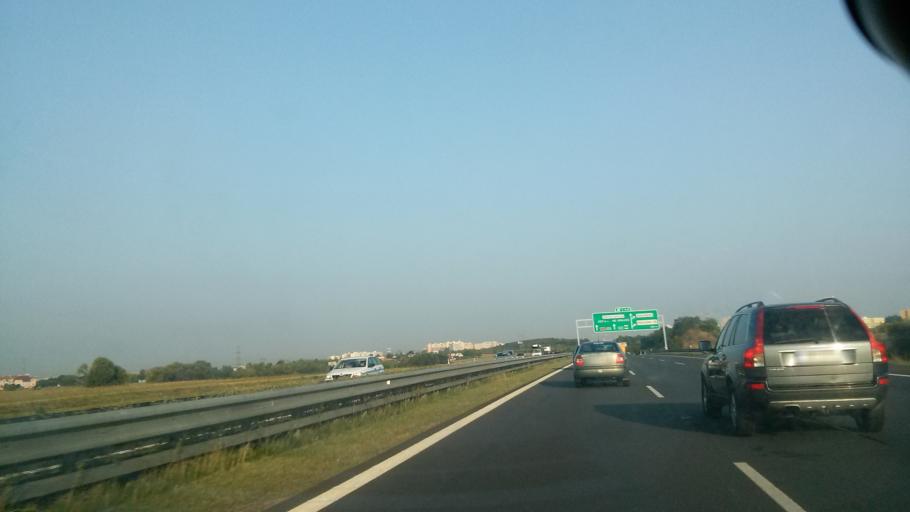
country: CZ
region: Central Bohemia
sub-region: Okres Praha-Zapad
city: Pruhonice
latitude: 50.0141
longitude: 14.5302
